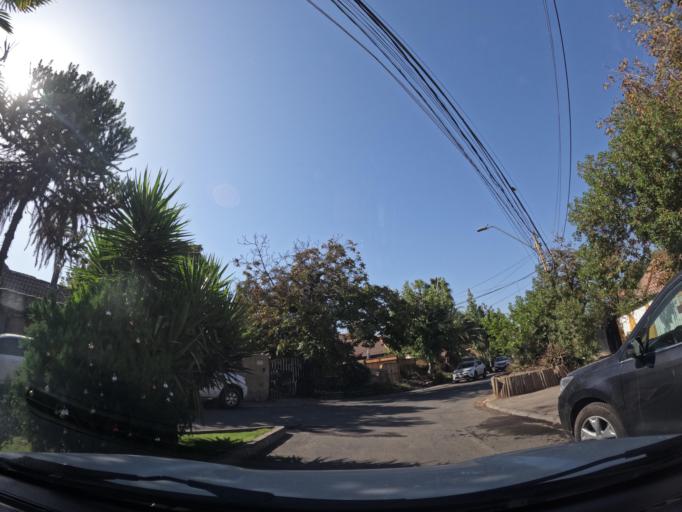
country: CL
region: Santiago Metropolitan
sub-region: Provincia de Santiago
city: Villa Presidente Frei, Nunoa, Santiago, Chile
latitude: -33.5060
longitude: -70.5569
